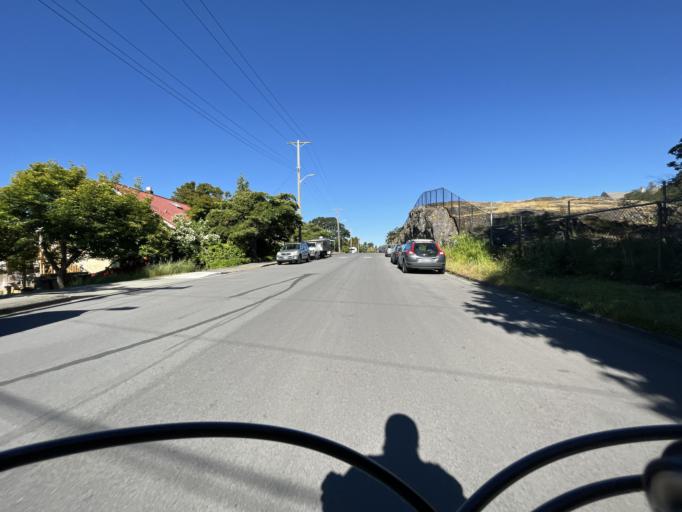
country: CA
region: British Columbia
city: Victoria
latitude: 48.4162
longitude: -123.3390
